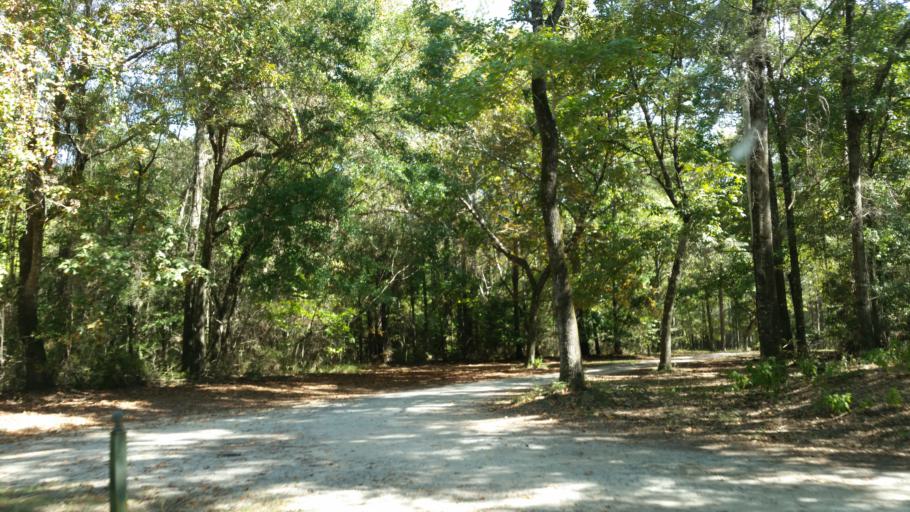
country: US
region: Alabama
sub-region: Baldwin County
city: Spanish Fort
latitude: 30.7477
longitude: -87.9180
